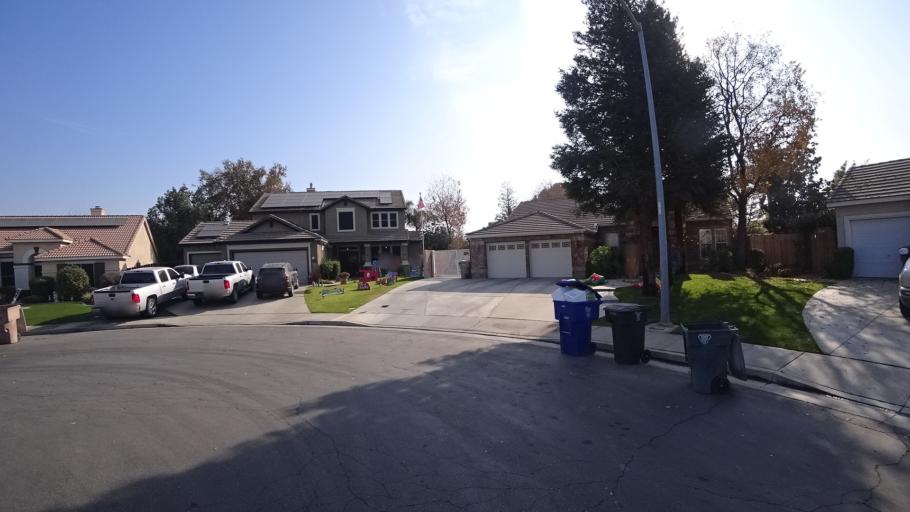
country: US
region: California
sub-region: Kern County
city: Greenacres
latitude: 35.4112
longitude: -119.1136
